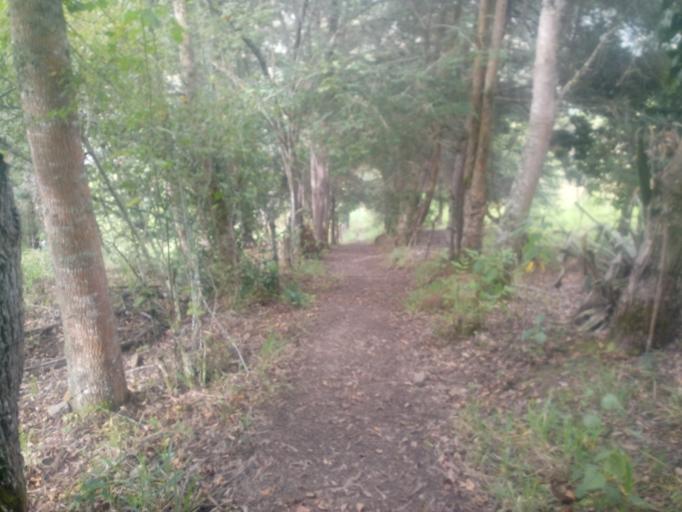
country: CO
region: Cundinamarca
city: Tenza
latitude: 5.0730
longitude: -73.4212
